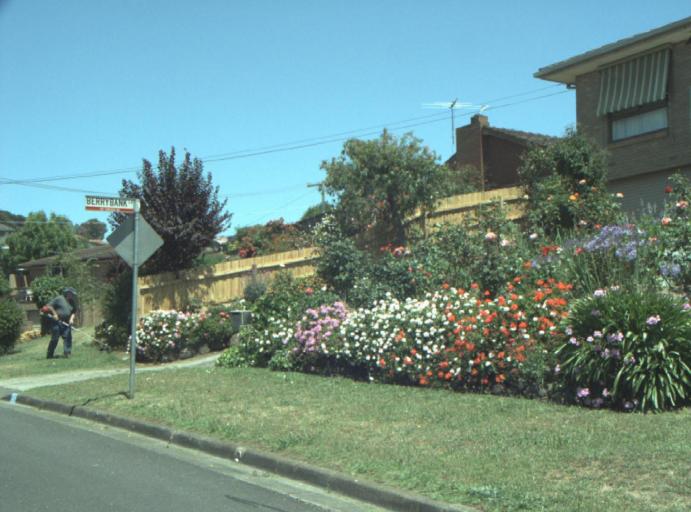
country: AU
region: Victoria
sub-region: Greater Geelong
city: Wandana Heights
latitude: -38.1600
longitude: 144.3191
